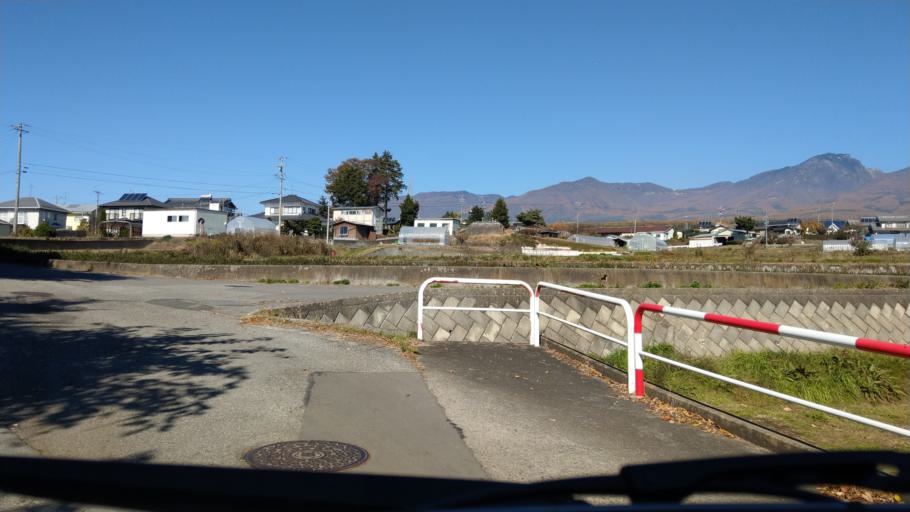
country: JP
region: Nagano
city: Komoro
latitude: 36.3194
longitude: 138.4619
